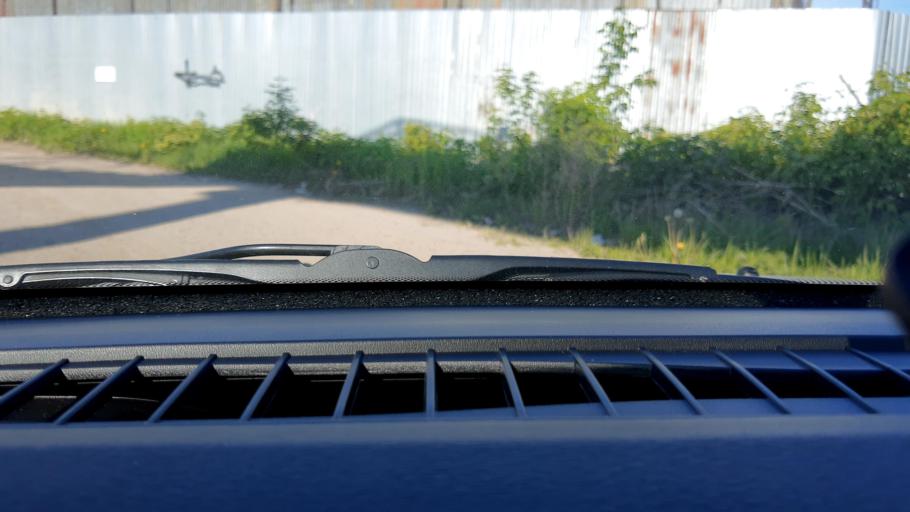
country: RU
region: Nizjnij Novgorod
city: Nizhniy Novgorod
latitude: 56.3068
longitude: 43.8850
